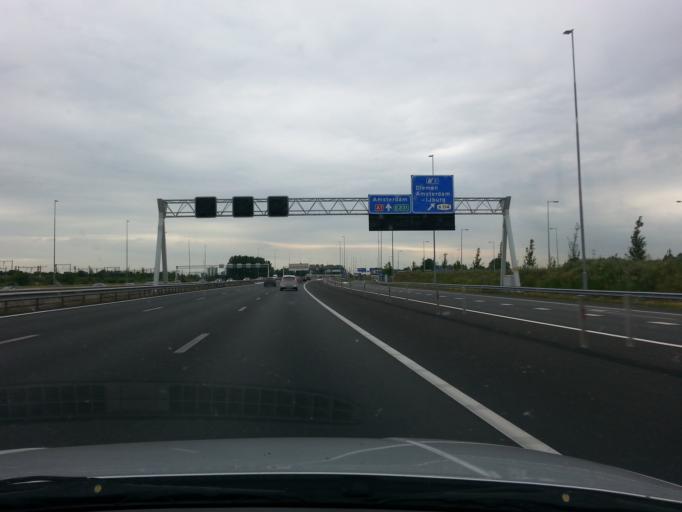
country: NL
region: North Holland
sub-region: Gemeente Diemen
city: Diemen
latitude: 52.3353
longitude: 4.9947
